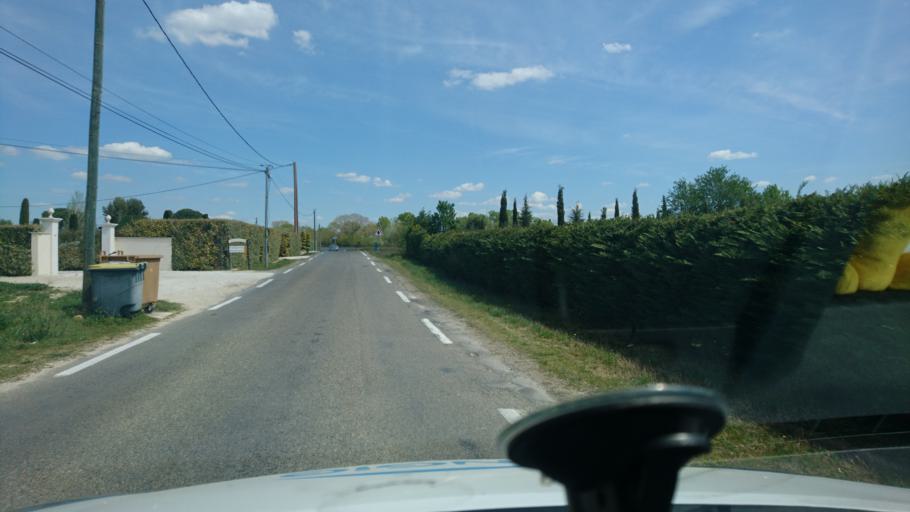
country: FR
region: Provence-Alpes-Cote d'Azur
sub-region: Departement du Vaucluse
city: Maubec
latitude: 43.8585
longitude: 5.1591
